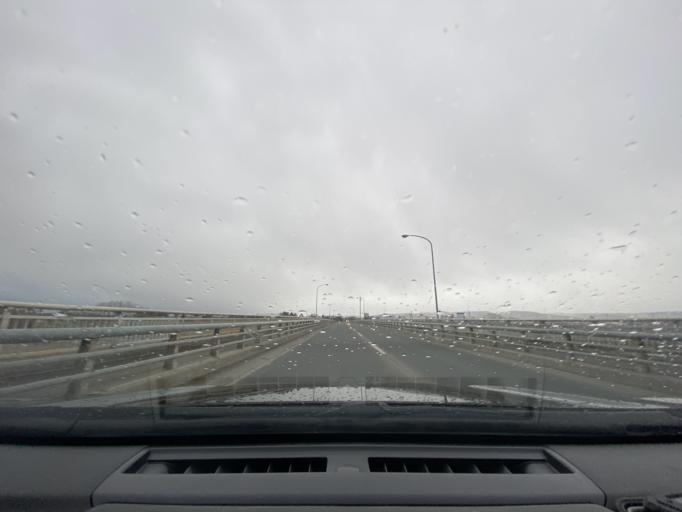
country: JP
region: Hokkaido
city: Kitami
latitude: 43.7988
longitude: 143.9126
